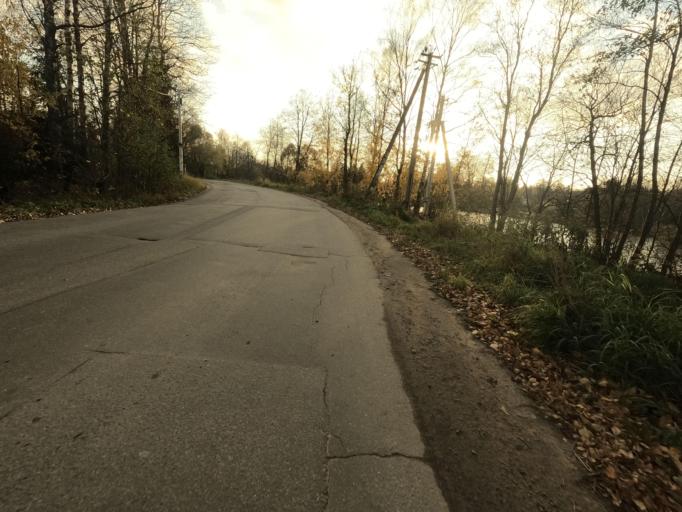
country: RU
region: St.-Petersburg
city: Beloostrov
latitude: 60.1721
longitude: 30.0140
